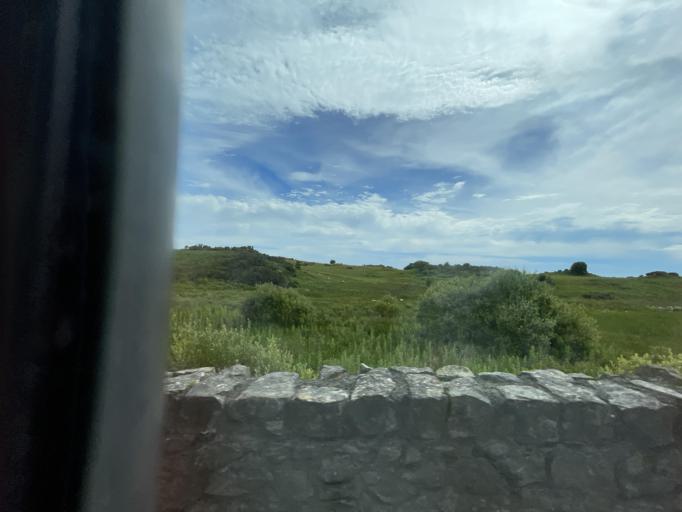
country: GB
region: Wales
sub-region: Anglesey
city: Llanfachraeth
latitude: 53.2601
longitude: -4.4300
